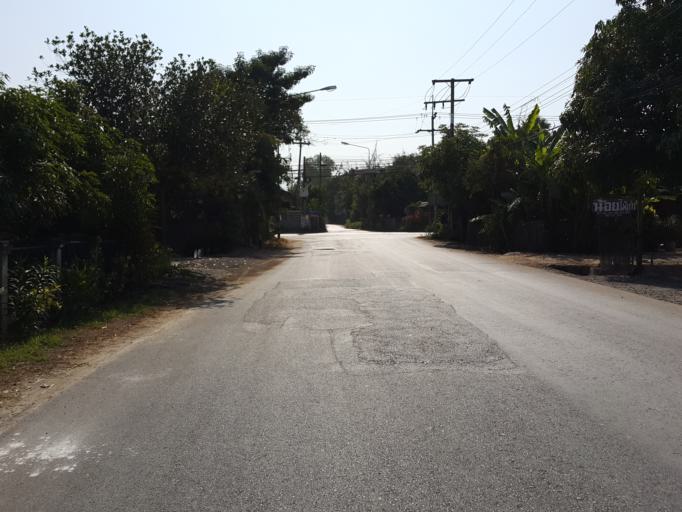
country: TH
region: Lamphun
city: Ban Thi
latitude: 18.6742
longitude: 99.1433
